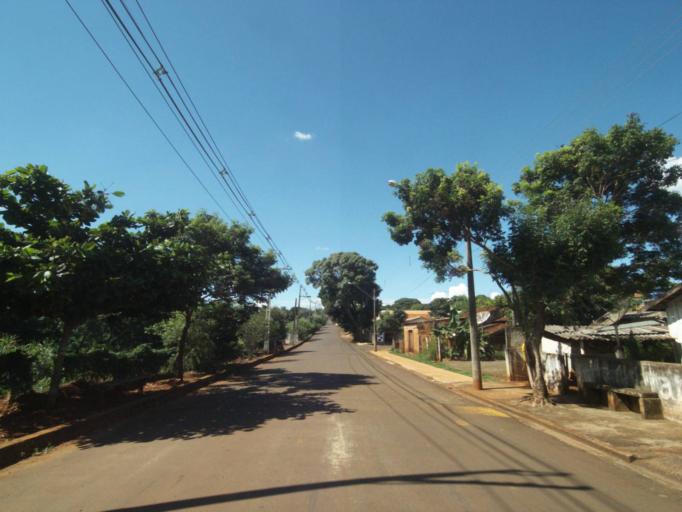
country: BR
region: Parana
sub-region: Sertanopolis
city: Sertanopolis
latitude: -23.0390
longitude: -50.8215
